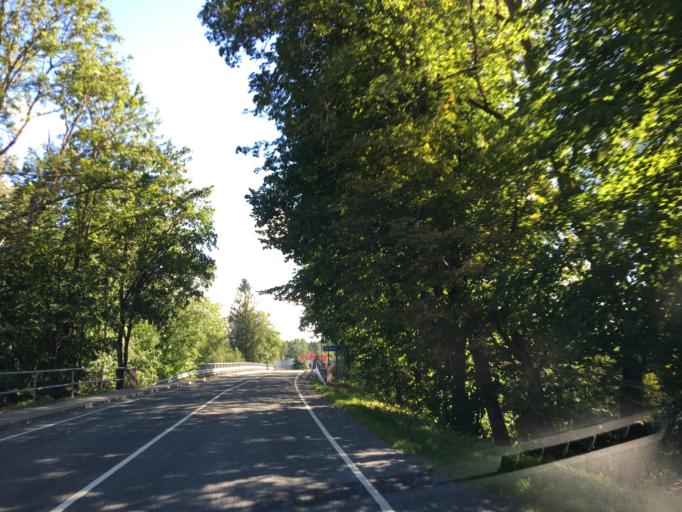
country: EE
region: Paernumaa
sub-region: Vaendra vald (alev)
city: Vandra
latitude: 58.6178
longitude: 25.1033
